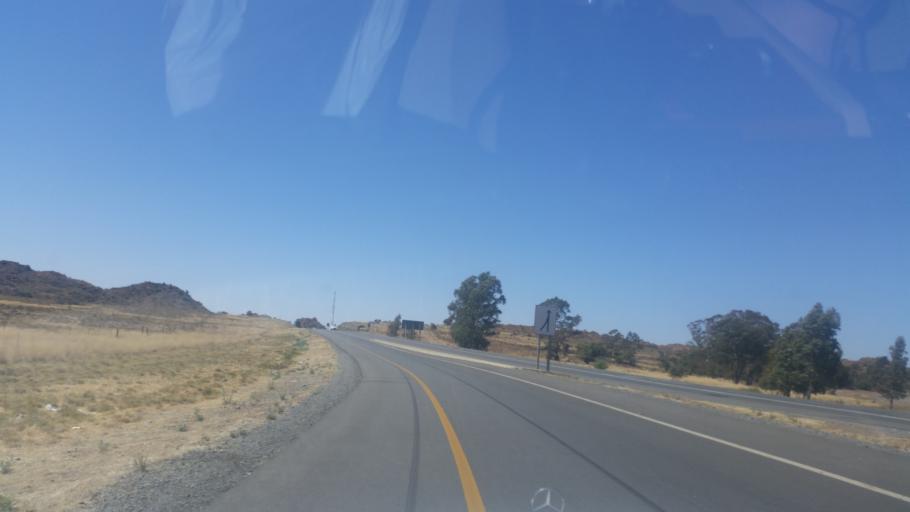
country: ZA
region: Northern Cape
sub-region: Pixley ka Seme District Municipality
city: Colesberg
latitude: -30.7241
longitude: 25.0877
